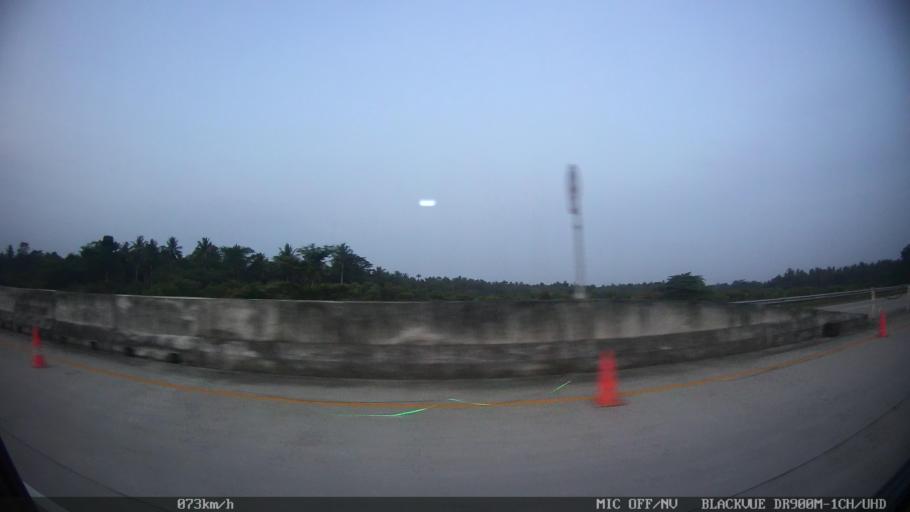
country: ID
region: Lampung
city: Kalianda
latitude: -5.6580
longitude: 105.5892
